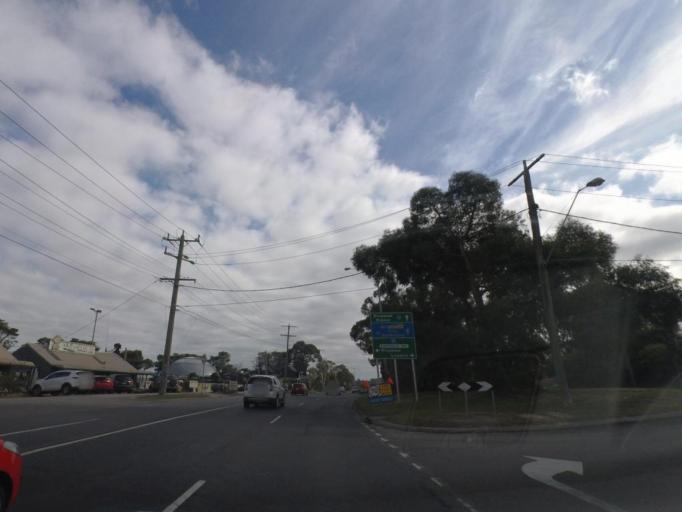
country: AU
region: Victoria
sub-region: Maroondah
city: Ringwood East
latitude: -37.8118
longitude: 145.2411
